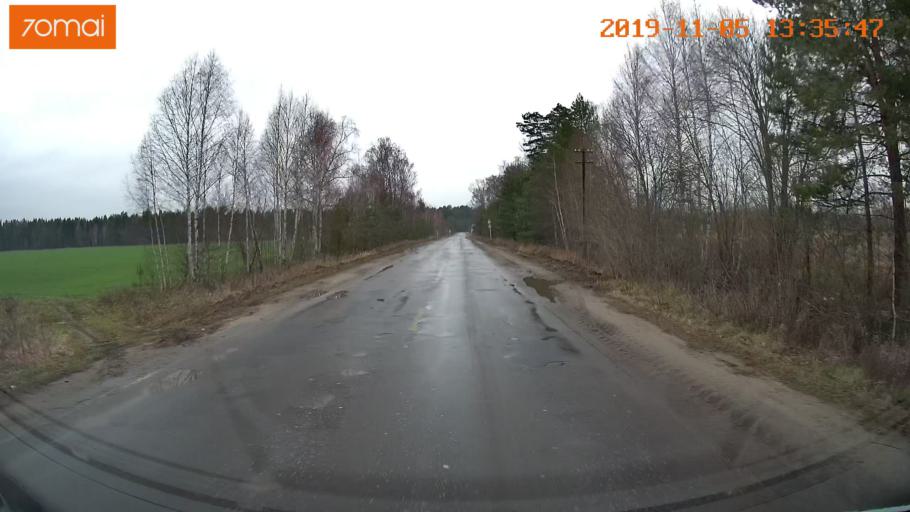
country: RU
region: Ivanovo
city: Shuya
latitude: 56.9102
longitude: 41.3855
